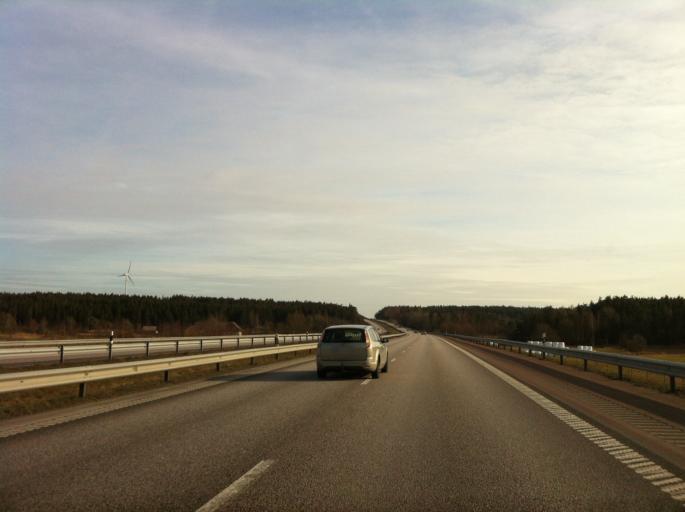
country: SE
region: Halland
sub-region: Kungsbacka Kommun
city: Fjaeras kyrkby
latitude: 57.4151
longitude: 12.1699
